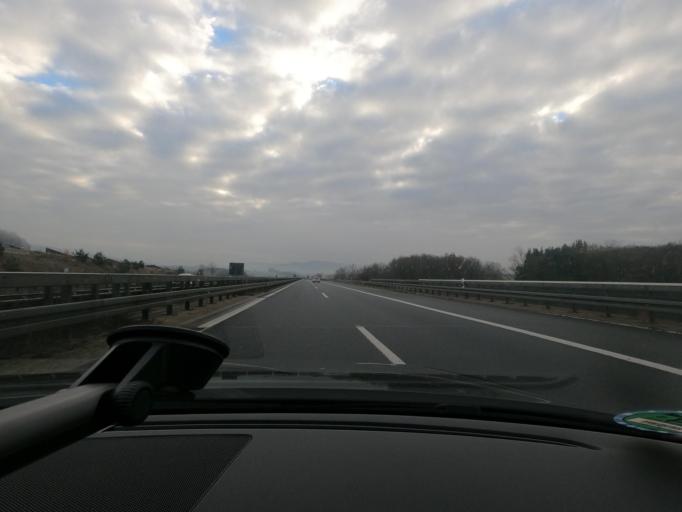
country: DE
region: Bavaria
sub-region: Upper Franconia
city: Lichtenfels
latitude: 50.1597
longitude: 11.0144
